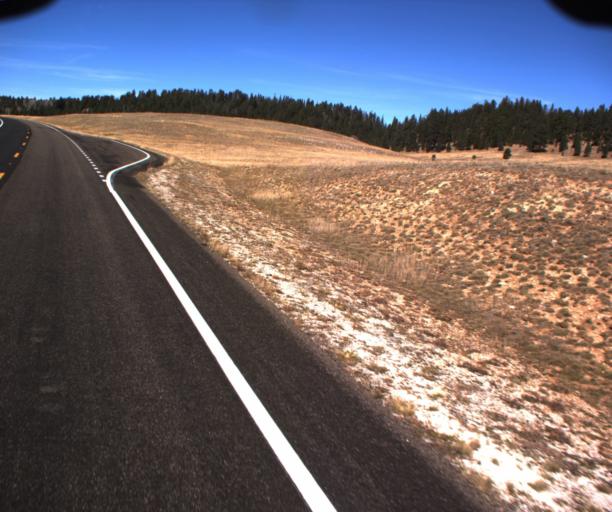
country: US
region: Arizona
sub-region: Coconino County
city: Grand Canyon
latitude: 36.4955
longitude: -112.1323
